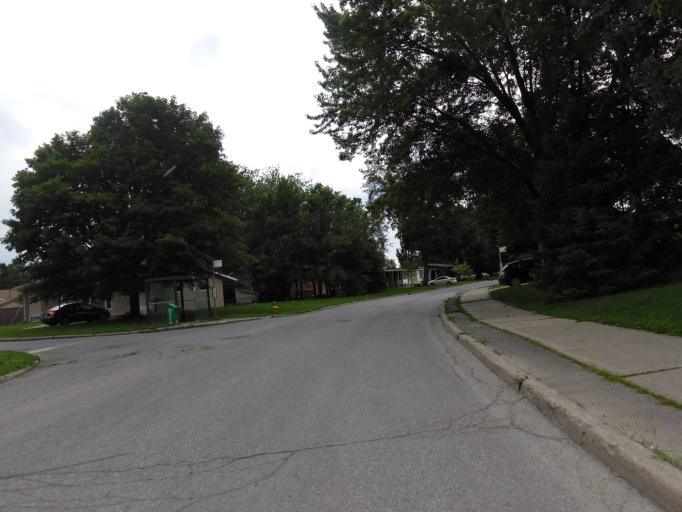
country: CA
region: Ontario
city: Bells Corners
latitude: 45.3478
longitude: -75.8345
